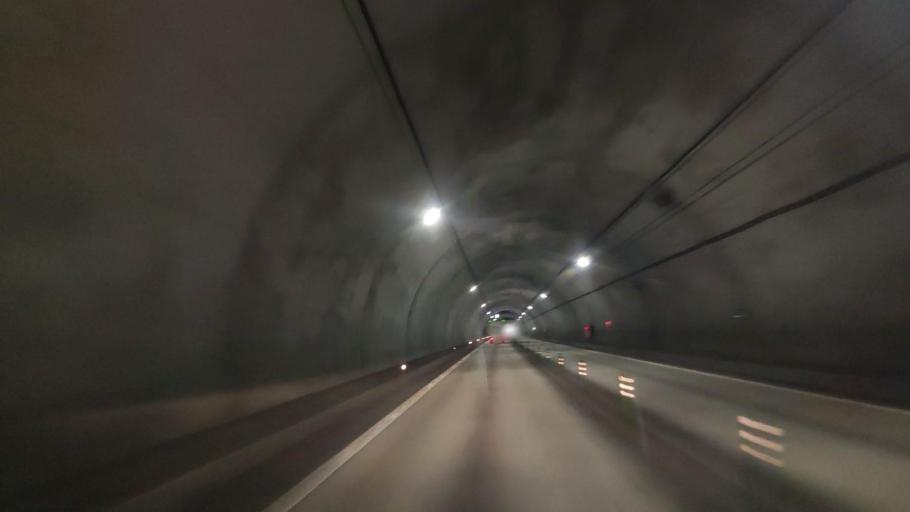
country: JP
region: Ishikawa
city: Nanao
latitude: 37.0197
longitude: 137.0082
